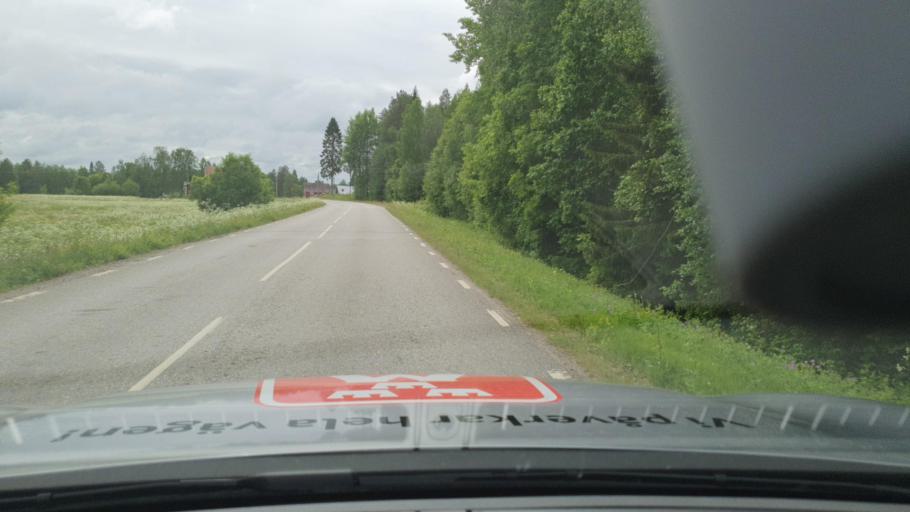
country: SE
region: Norrbotten
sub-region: Lulea Kommun
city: Ranea
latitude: 65.9203
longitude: 22.1499
